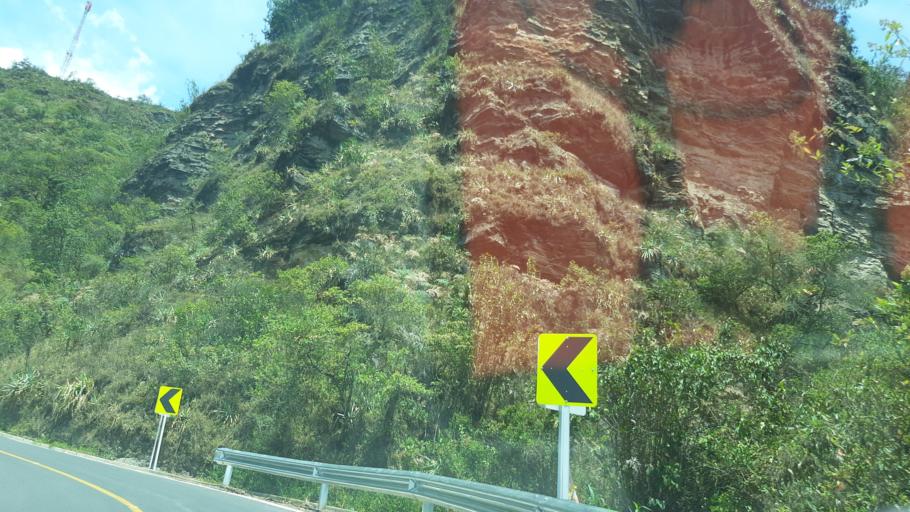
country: CO
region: Boyaca
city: Chinavita
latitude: 5.1321
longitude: -73.3884
